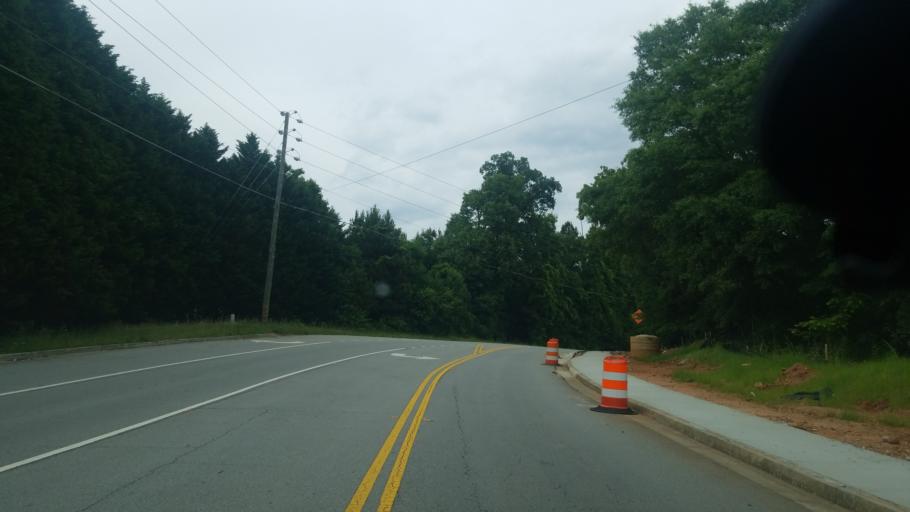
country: US
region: Georgia
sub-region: Forsyth County
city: Cumming
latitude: 34.1785
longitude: -84.1297
